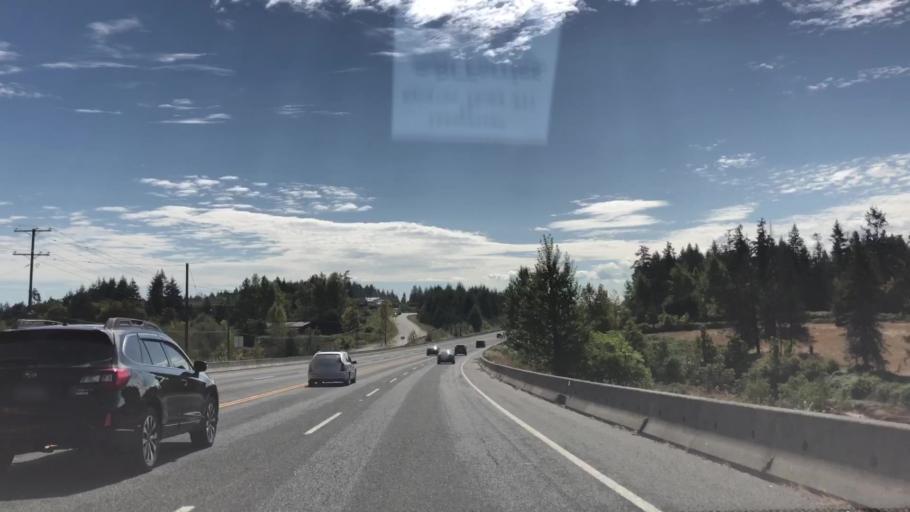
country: CA
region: British Columbia
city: Nanaimo
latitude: 49.1301
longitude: -123.8653
